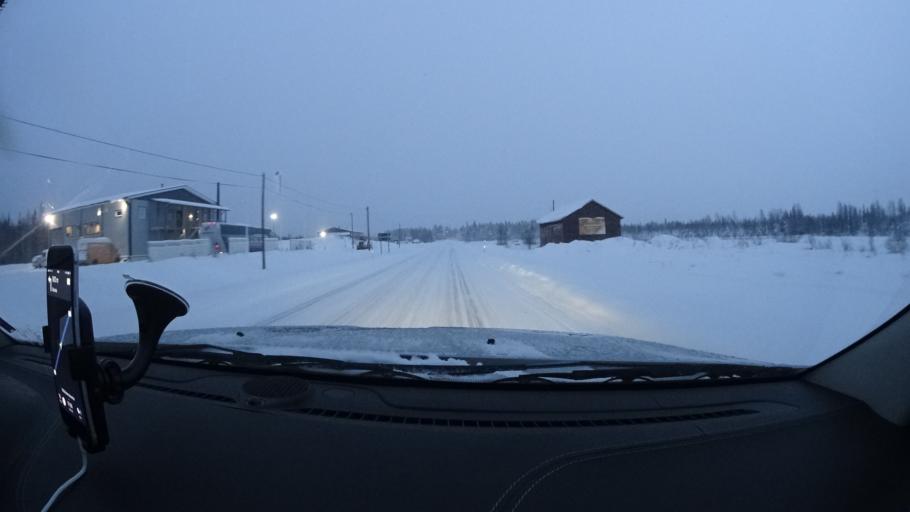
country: FI
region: Lapland
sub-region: Tunturi-Lappi
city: Kittilae
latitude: 67.6679
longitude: 24.8641
